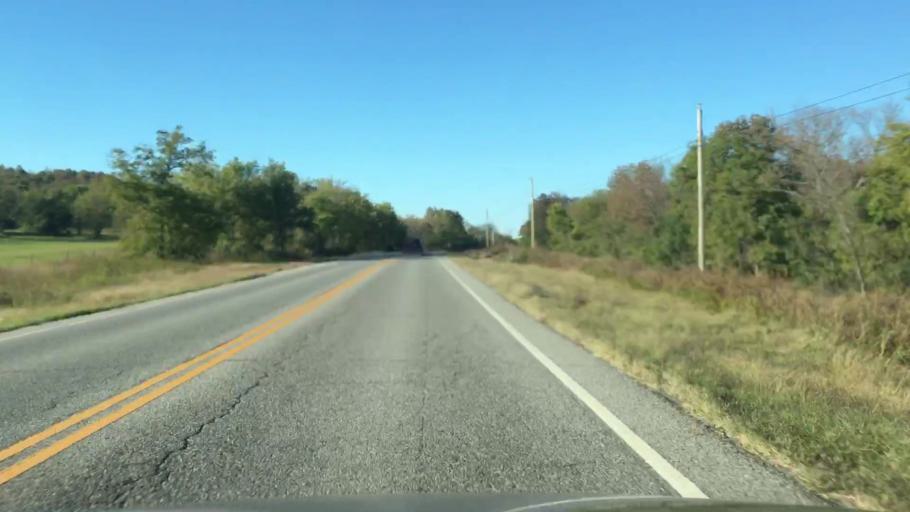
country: US
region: Oklahoma
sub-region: Cherokee County
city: Tahlequah
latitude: 35.9200
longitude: -95.1228
